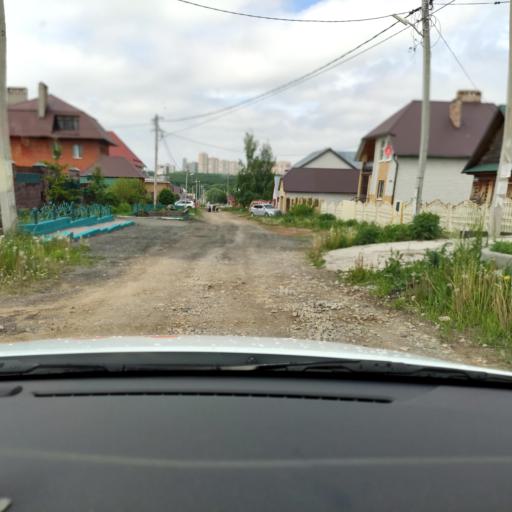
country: RU
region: Tatarstan
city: Stolbishchi
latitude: 55.7762
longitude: 49.2616
